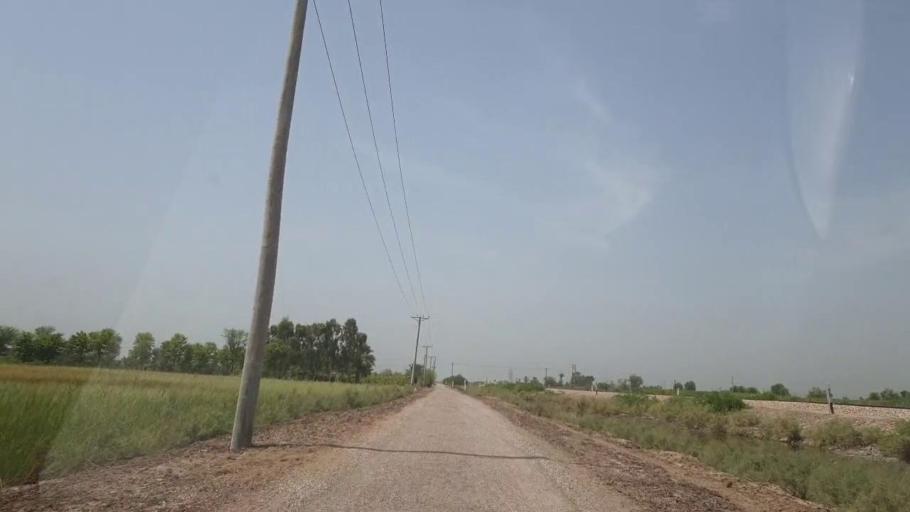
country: PK
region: Sindh
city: Gambat
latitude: 27.3221
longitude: 68.5371
